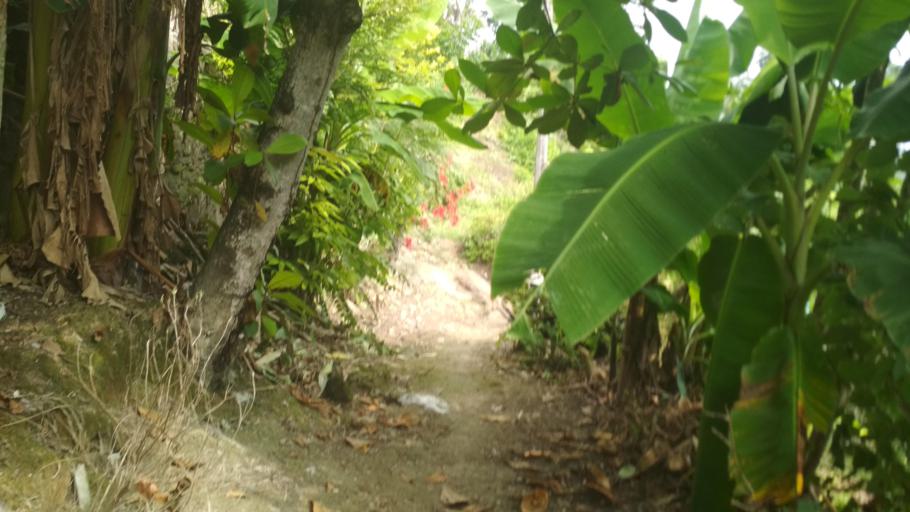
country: MX
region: Veracruz
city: Papantla de Olarte
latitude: 20.4800
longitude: -97.3582
